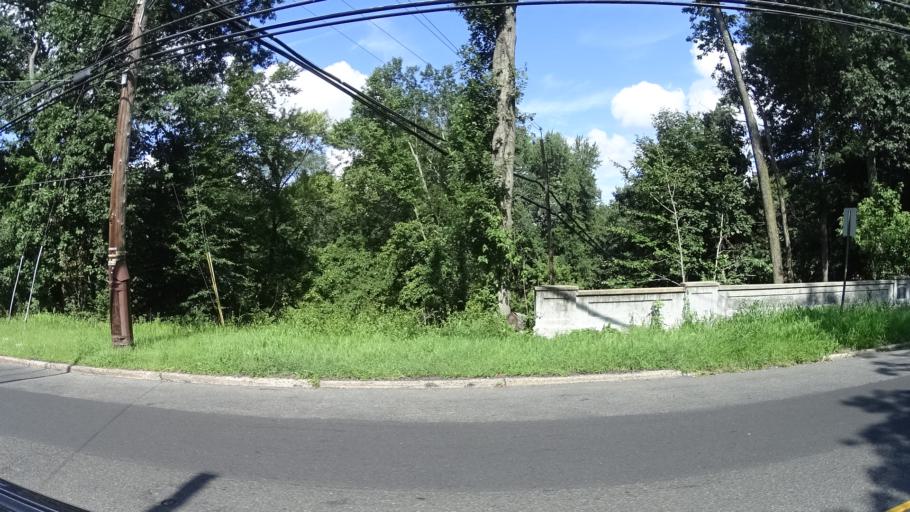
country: US
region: New Jersey
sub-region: Union County
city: Summit
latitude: 40.7346
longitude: -74.3707
